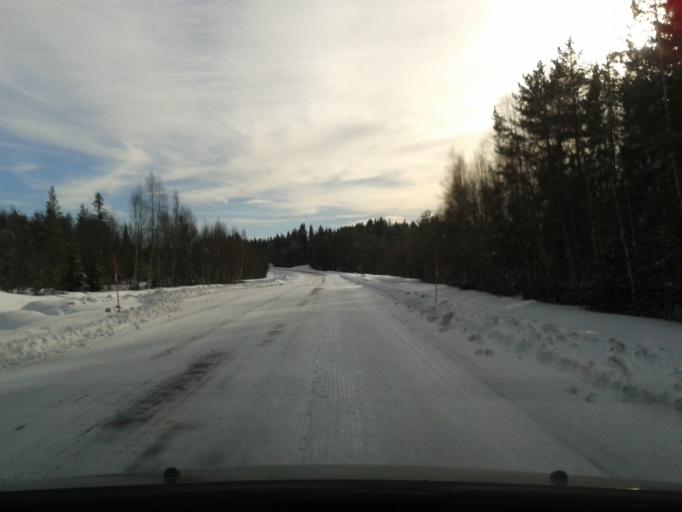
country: SE
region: Vaesterbotten
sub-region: Vilhelmina Kommun
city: Vilhelmina
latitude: 64.5417
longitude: 16.7470
